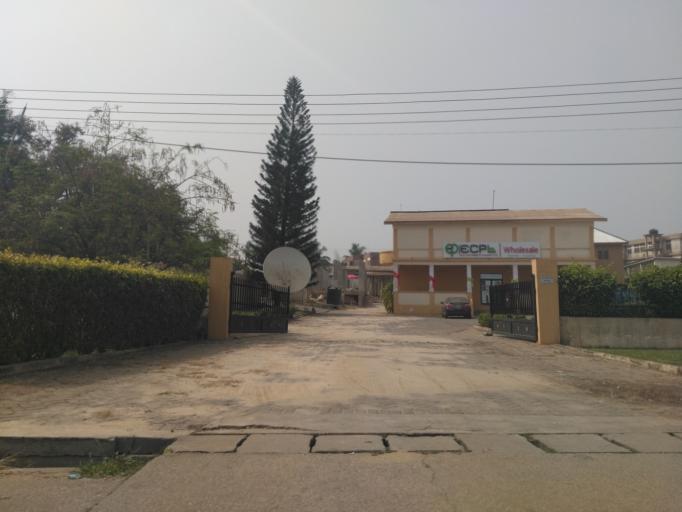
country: GH
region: Ashanti
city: Kumasi
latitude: 6.6730
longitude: -1.6044
